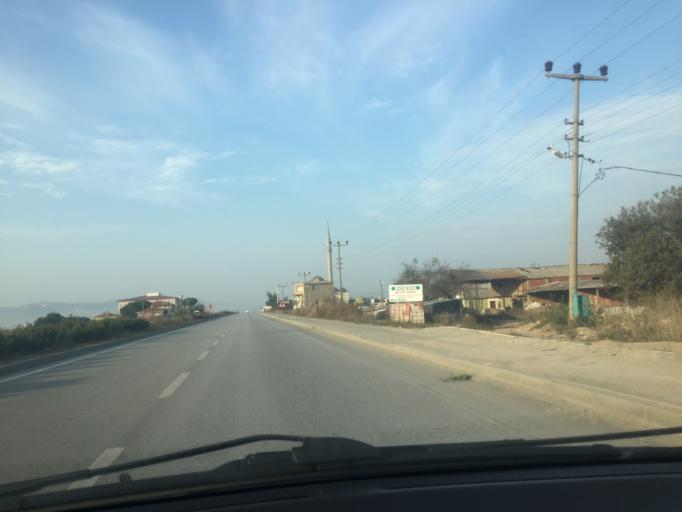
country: TR
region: Canakkale
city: Dimetoka
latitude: 40.2460
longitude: 27.2818
